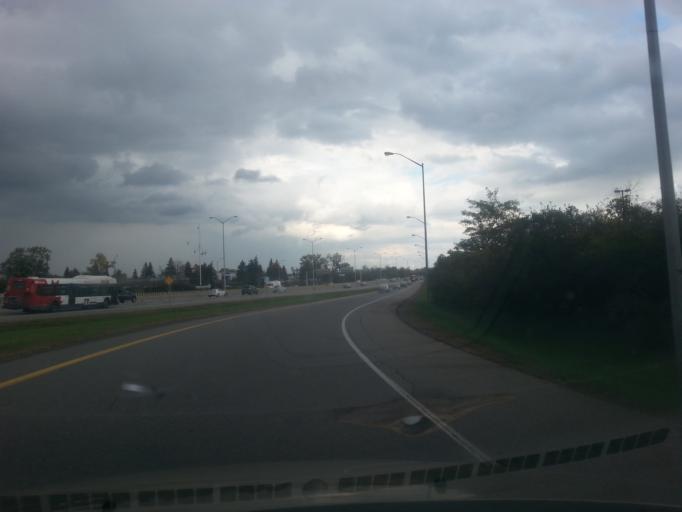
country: CA
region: Ontario
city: Bells Corners
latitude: 45.3495
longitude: -75.7888
